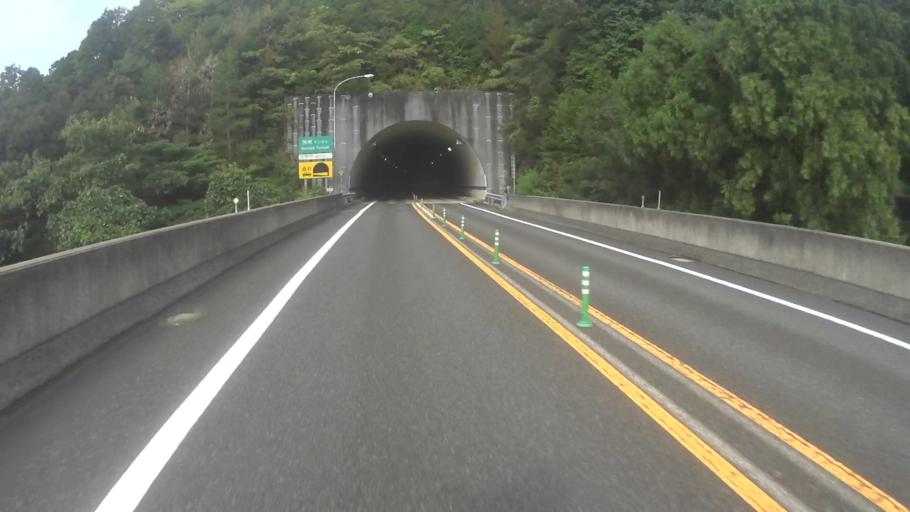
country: JP
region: Kyoto
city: Ayabe
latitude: 35.3754
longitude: 135.2675
